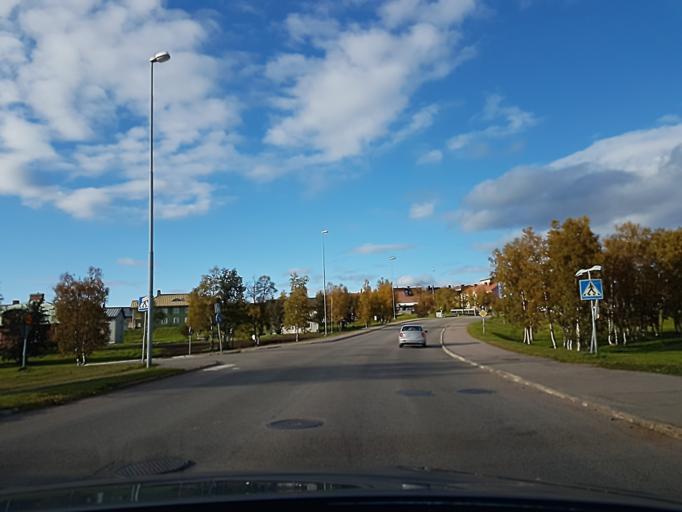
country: SE
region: Norrbotten
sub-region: Kiruna Kommun
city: Kiruna
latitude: 67.8455
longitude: 20.2308
